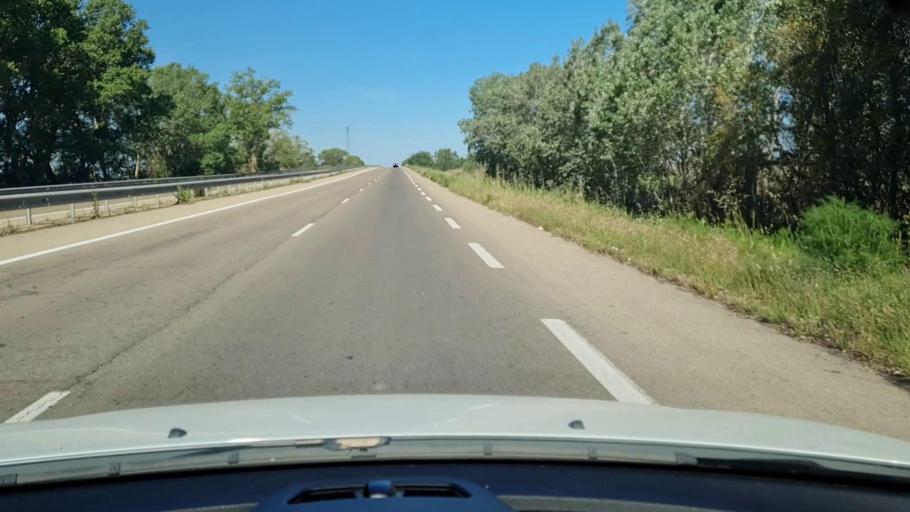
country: FR
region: Languedoc-Roussillon
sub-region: Departement du Gard
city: Le Grau-du-Roi
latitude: 43.5611
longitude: 4.1476
